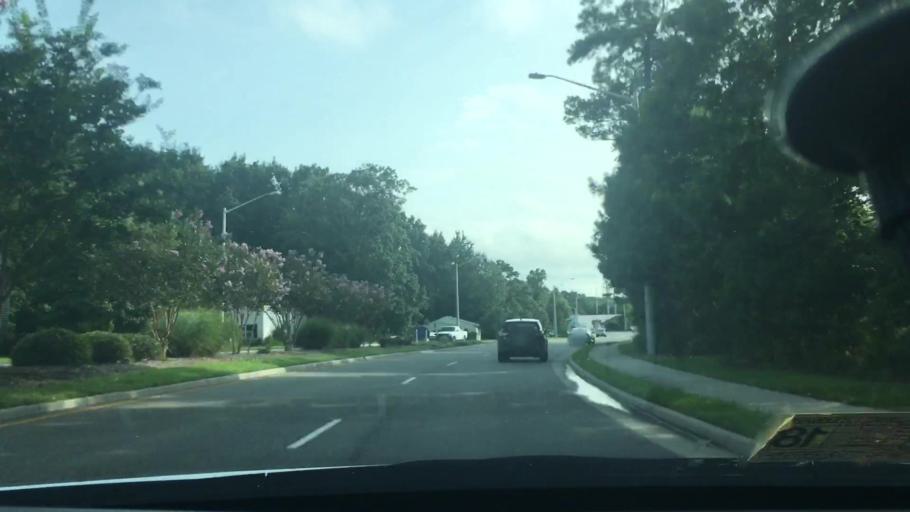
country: US
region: Virginia
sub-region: City of Virginia Beach
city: Virginia Beach
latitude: 36.8253
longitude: -75.9984
